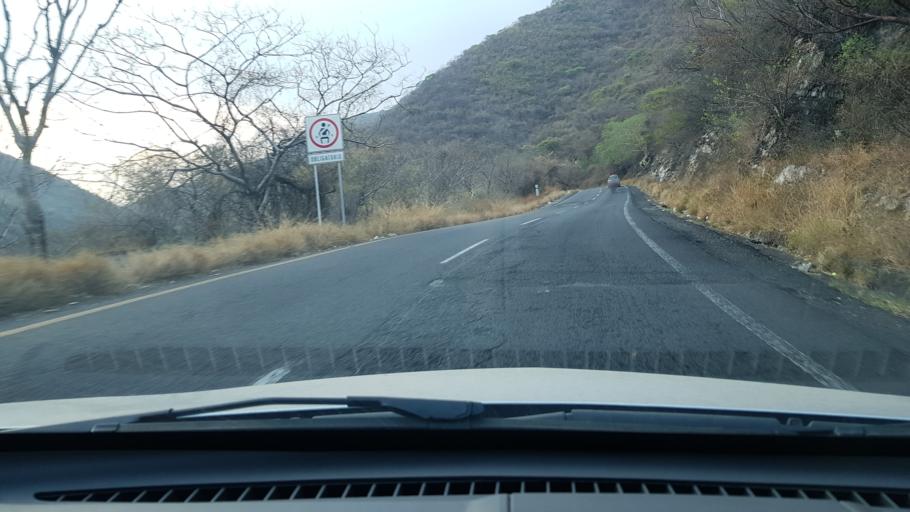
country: MX
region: Morelos
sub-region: Jiutepec
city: Independencia
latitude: 18.8586
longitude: -99.1172
